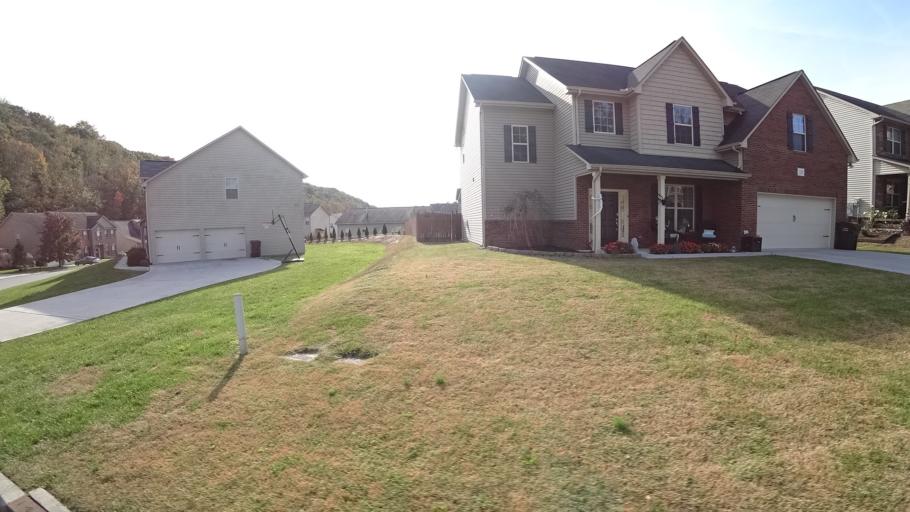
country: US
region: Tennessee
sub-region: Knox County
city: Farragut
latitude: 35.9129
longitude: -84.1815
